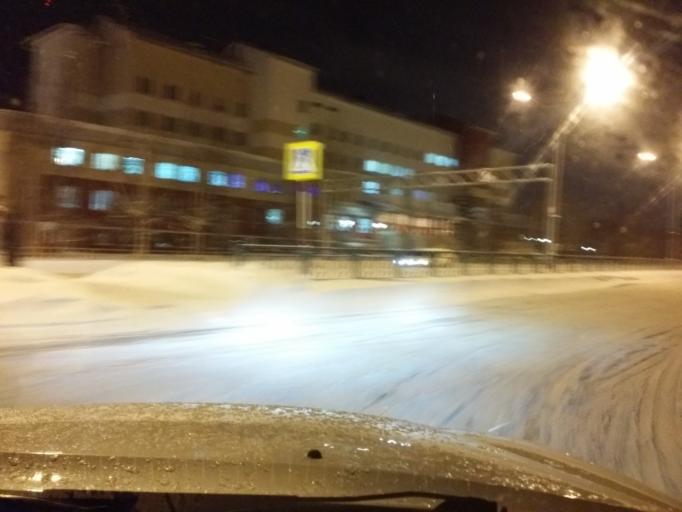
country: RU
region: Khanty-Mansiyskiy Avtonomnyy Okrug
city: Nizhnevartovsk
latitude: 60.9384
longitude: 76.5760
